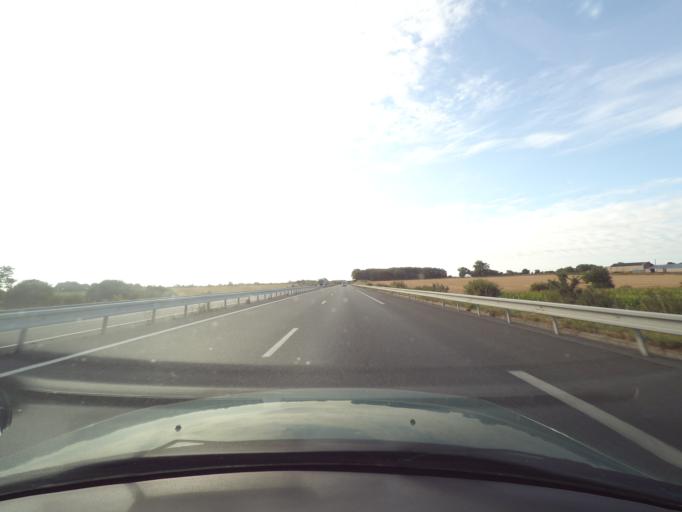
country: FR
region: Poitou-Charentes
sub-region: Departement des Deux-Sevres
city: Combrand
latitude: 46.9260
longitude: -0.7126
